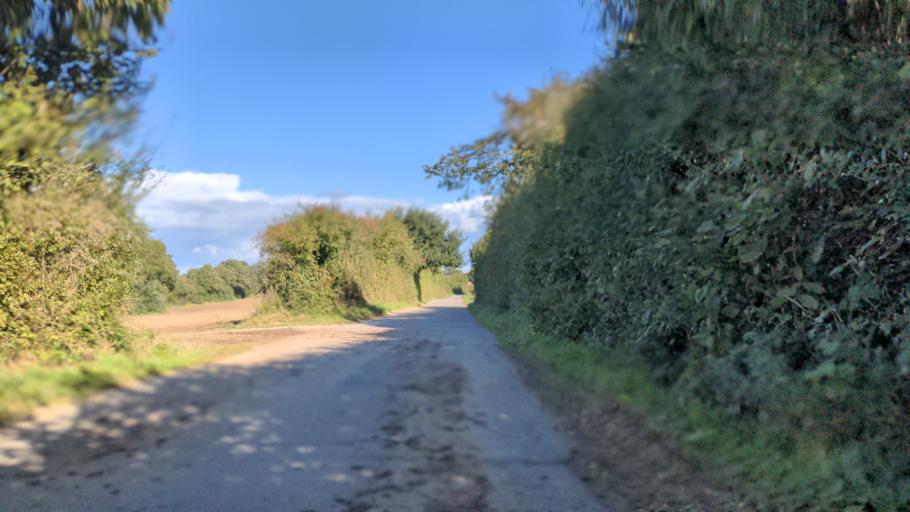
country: DE
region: Schleswig-Holstein
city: Manhagen
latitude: 54.1654
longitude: 10.9157
